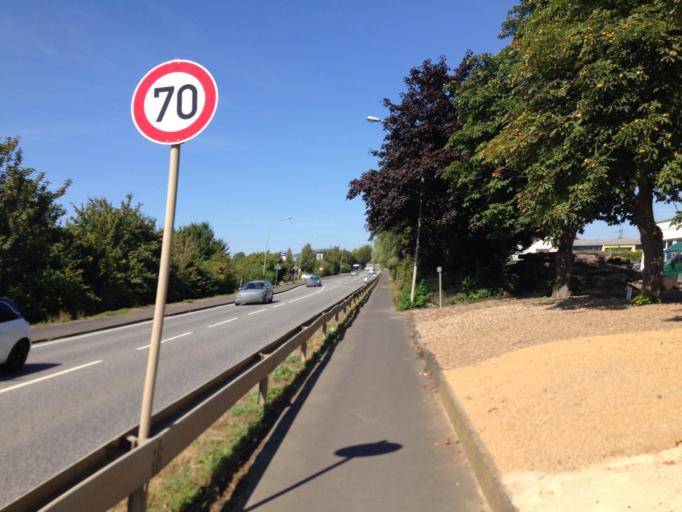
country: DE
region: Hesse
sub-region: Regierungsbezirk Giessen
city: Heuchelheim
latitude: 50.5999
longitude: 8.6265
